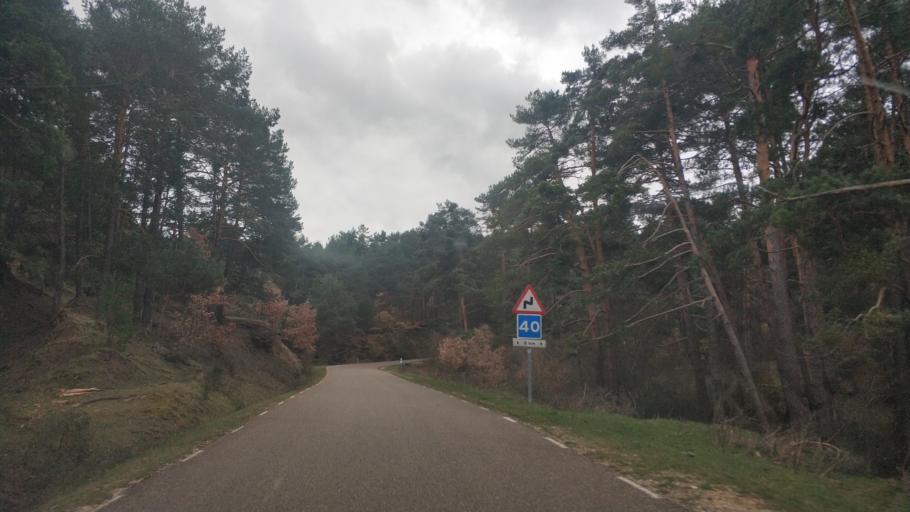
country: ES
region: Castille and Leon
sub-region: Provincia de Burgos
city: Canicosa de la Sierra
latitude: 41.9315
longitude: -3.0370
